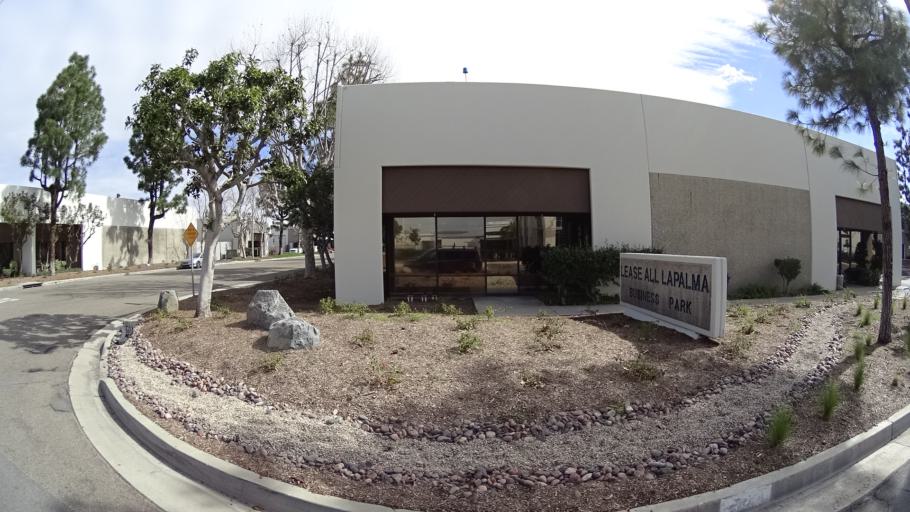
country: US
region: California
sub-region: Orange County
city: Yorba Linda
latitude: 33.8615
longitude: -117.8312
